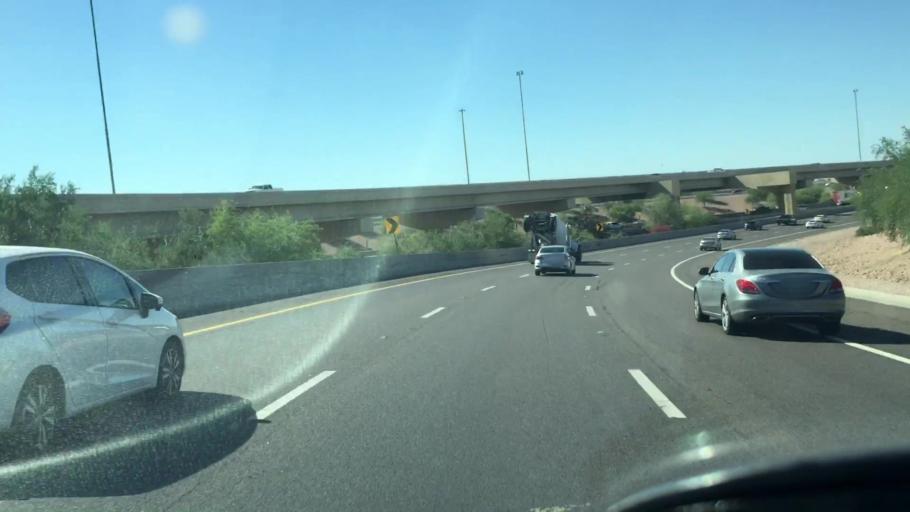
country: US
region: Arizona
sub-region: Maricopa County
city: Guadalupe
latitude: 33.3897
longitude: -111.9651
